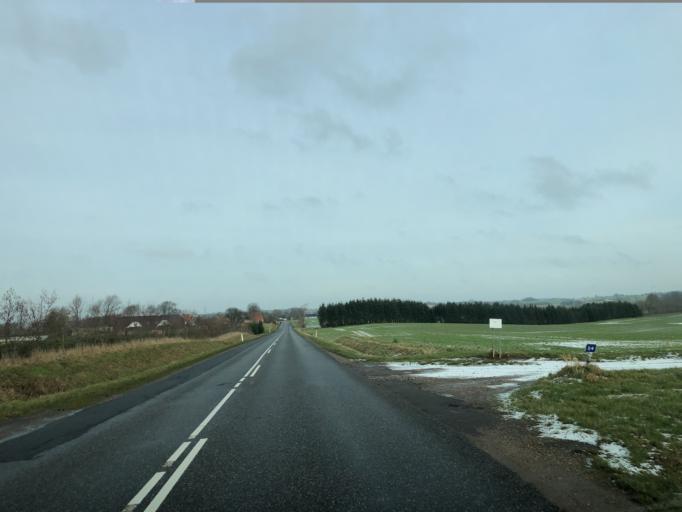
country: DK
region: South Denmark
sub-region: Vejle Kommune
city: Jelling
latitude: 55.7905
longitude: 9.4432
